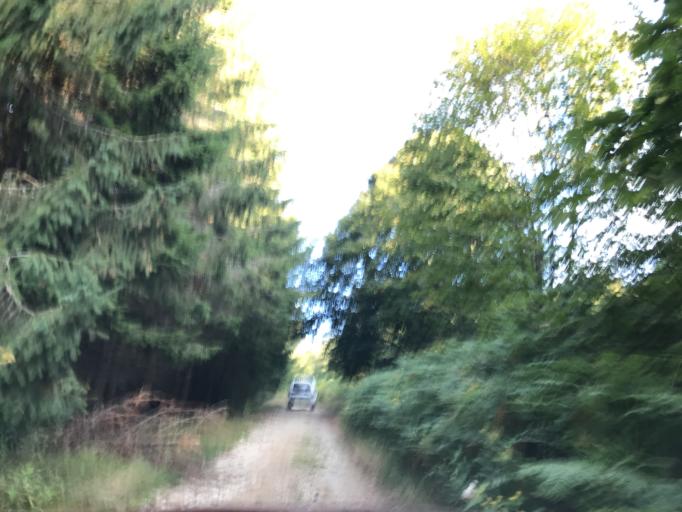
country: FR
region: Rhone-Alpes
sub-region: Departement de la Loire
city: Noiretable
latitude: 45.7630
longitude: 3.7522
